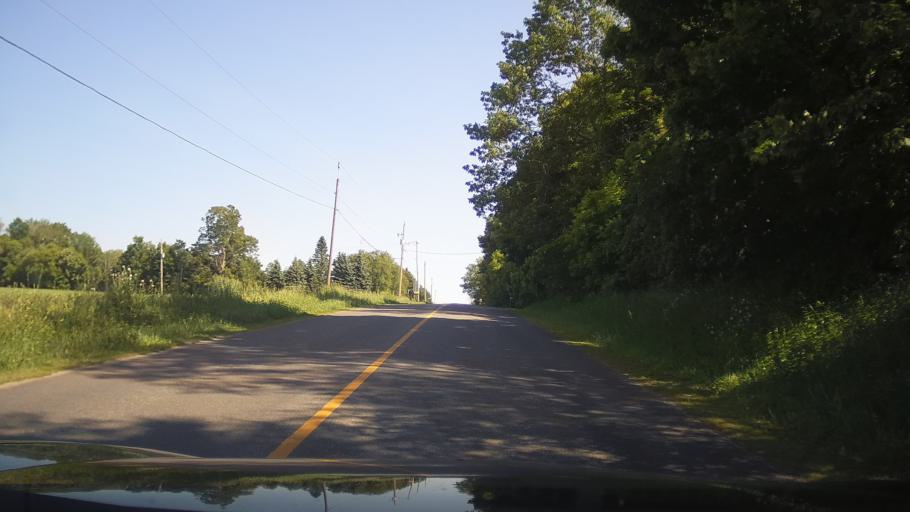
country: CA
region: Ontario
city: Oshawa
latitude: 43.9504
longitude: -78.7248
